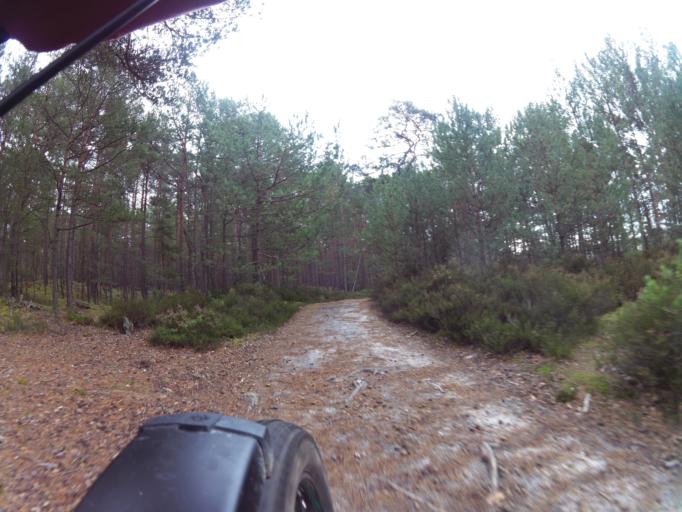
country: PL
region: Pomeranian Voivodeship
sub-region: Powiat pucki
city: Hel
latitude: 54.6268
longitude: 18.8029
